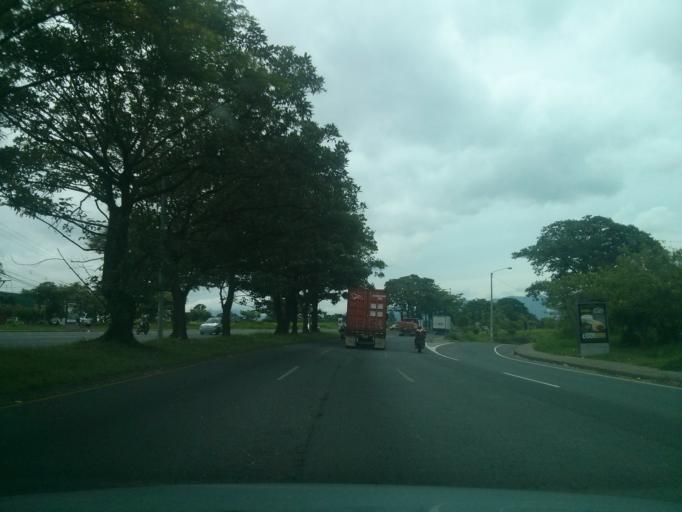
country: CR
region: San Jose
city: San Felipe
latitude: 9.9239
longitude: -84.1090
